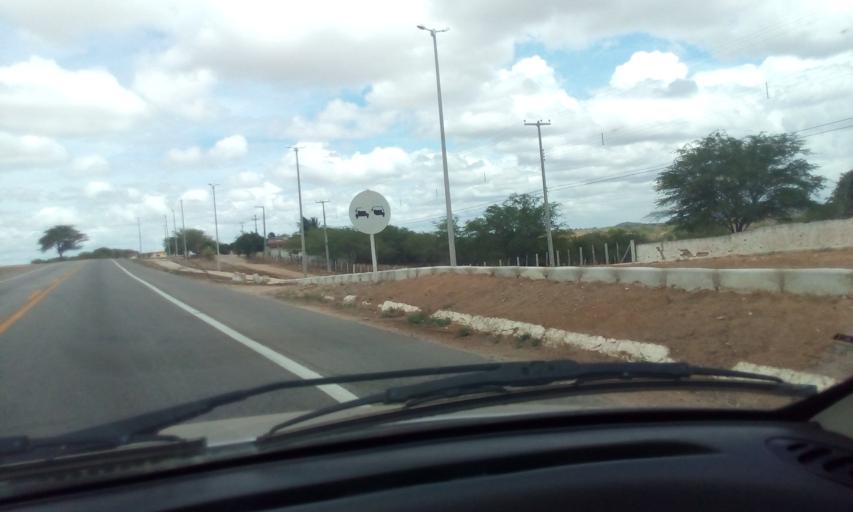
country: BR
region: Rio Grande do Norte
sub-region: Tangara
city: Tangara
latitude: -6.1922
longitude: -35.7918
